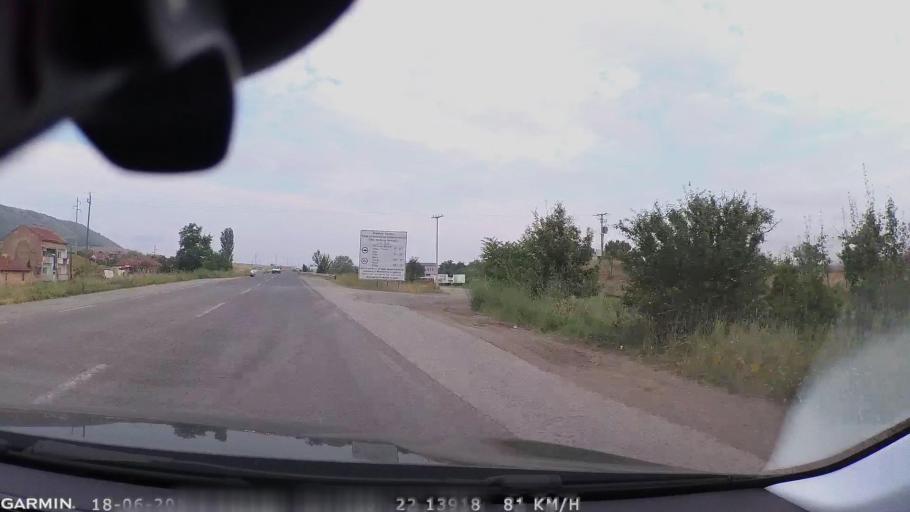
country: MK
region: Stip
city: Shtip
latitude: 41.7744
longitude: 22.1383
